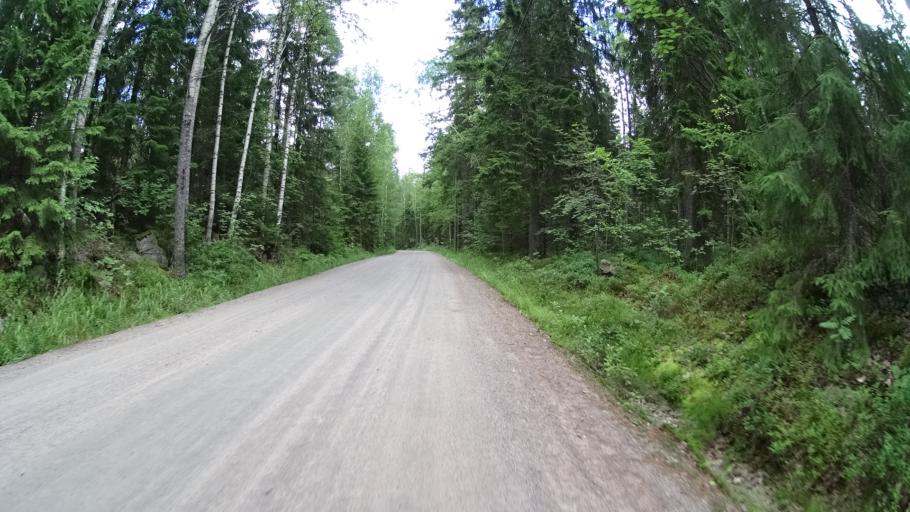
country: FI
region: Uusimaa
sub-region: Helsinki
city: Espoo
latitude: 60.2932
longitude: 24.6162
